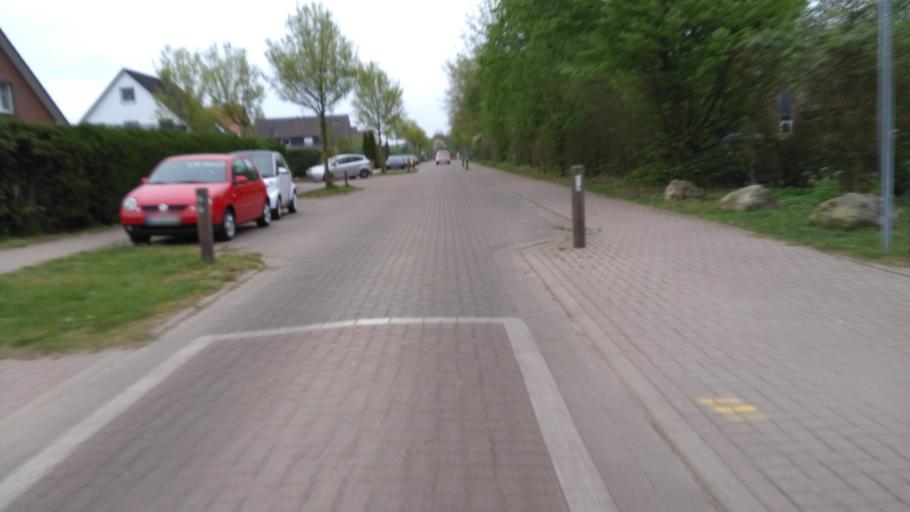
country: DE
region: Lower Saxony
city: Harsefeld
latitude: 53.4528
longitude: 9.5191
